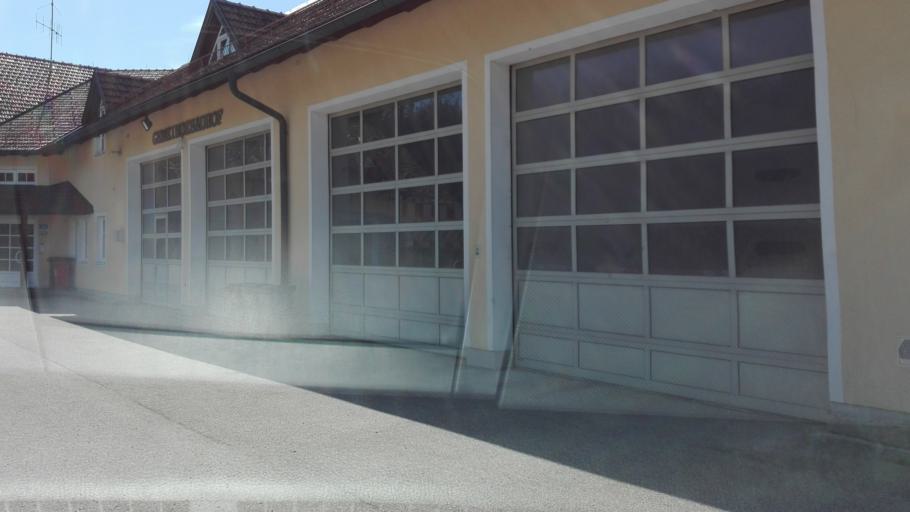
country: AT
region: Upper Austria
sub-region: Politischer Bezirk Grieskirchen
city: Grieskirchen
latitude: 48.2140
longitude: 13.7807
